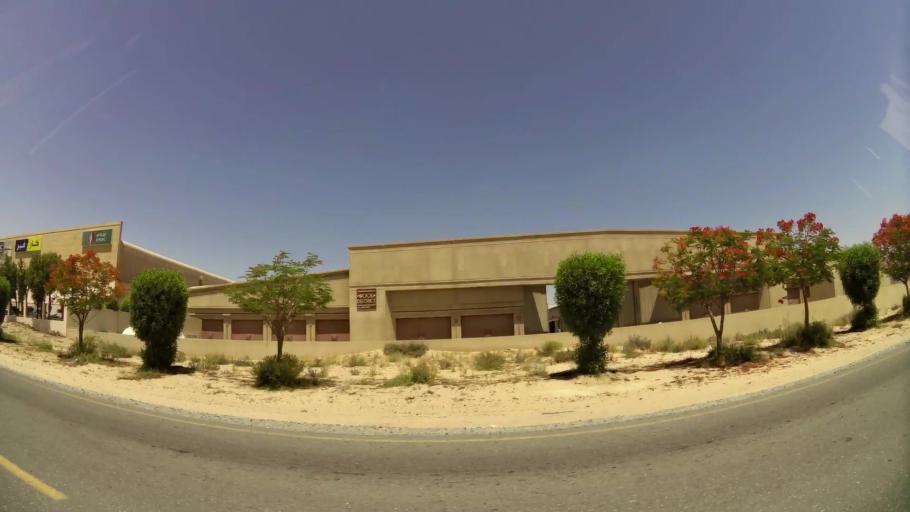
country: AE
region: Dubai
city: Dubai
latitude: 24.9770
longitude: 55.1880
